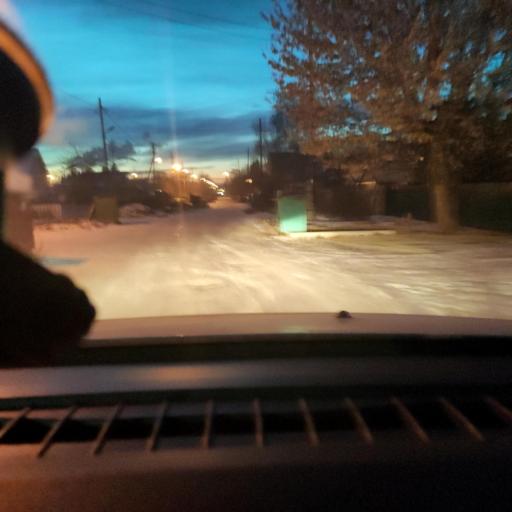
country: RU
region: Samara
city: Petra-Dubrava
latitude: 53.2583
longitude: 50.3370
